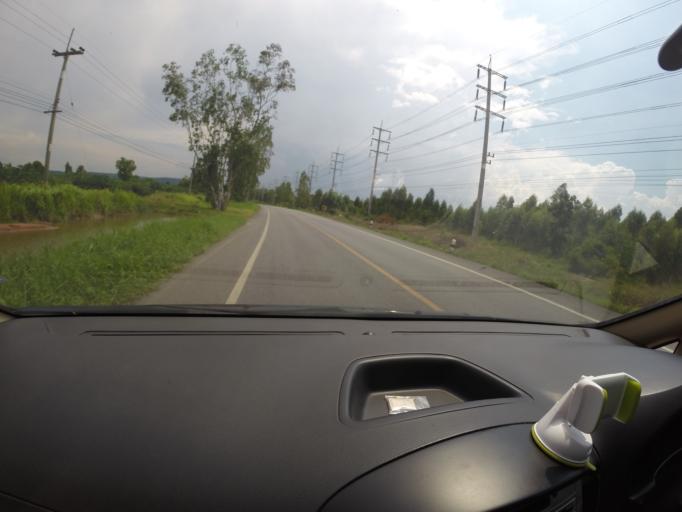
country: TH
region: Nakhon Ratchasima
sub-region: Amphoe Thepharak
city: Thepharak
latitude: 15.1159
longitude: 101.4677
